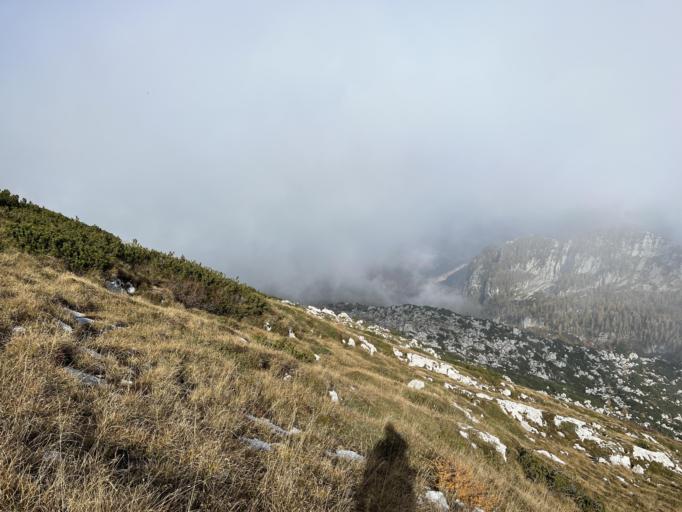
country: IT
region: Friuli Venezia Giulia
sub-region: Provincia di Pordenone
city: Andreis
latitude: 46.2191
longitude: 12.6529
